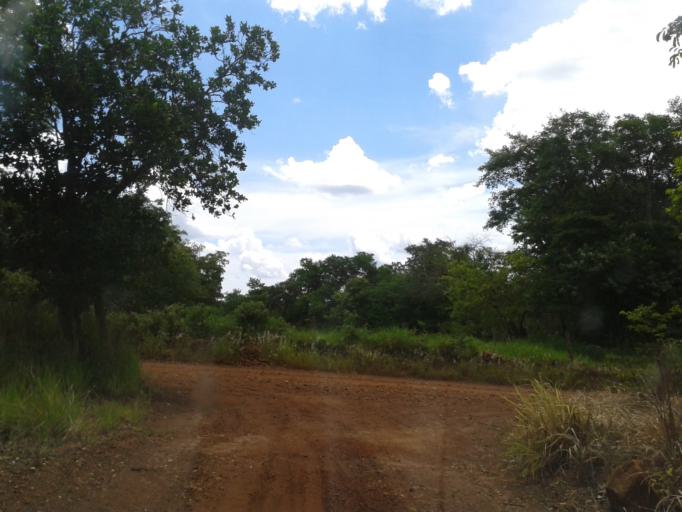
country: BR
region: Minas Gerais
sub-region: Centralina
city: Centralina
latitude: -18.6842
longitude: -49.2247
